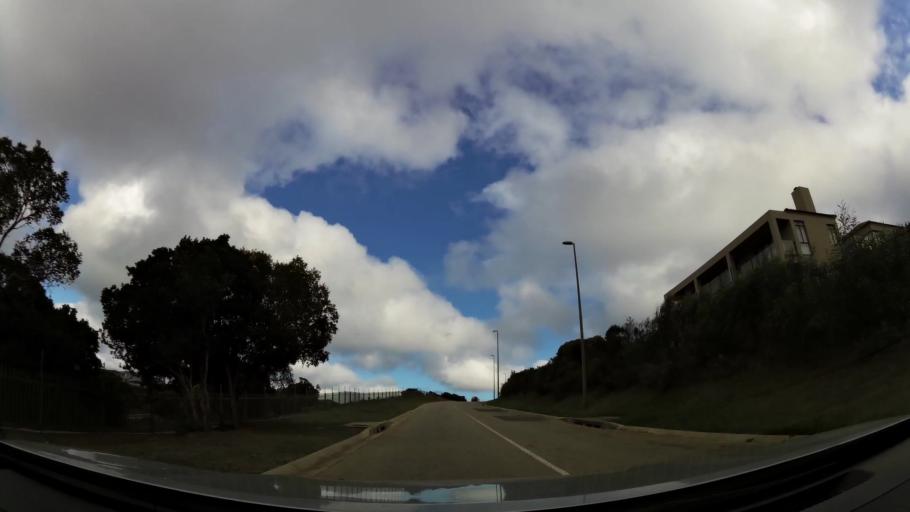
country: ZA
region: Western Cape
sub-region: Eden District Municipality
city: Plettenberg Bay
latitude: -34.0878
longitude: 23.3559
